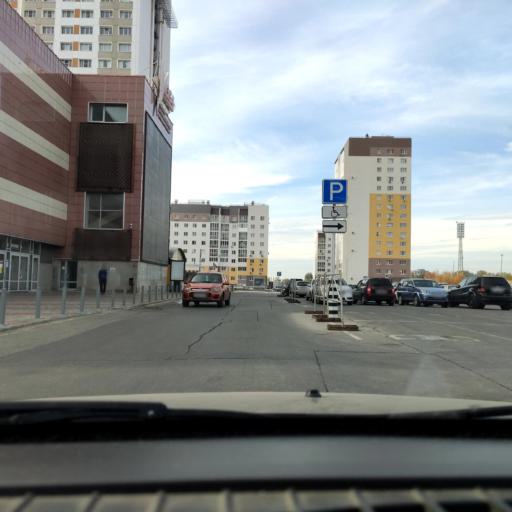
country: RU
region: Samara
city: Tol'yatti
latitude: 53.5015
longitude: 49.2741
